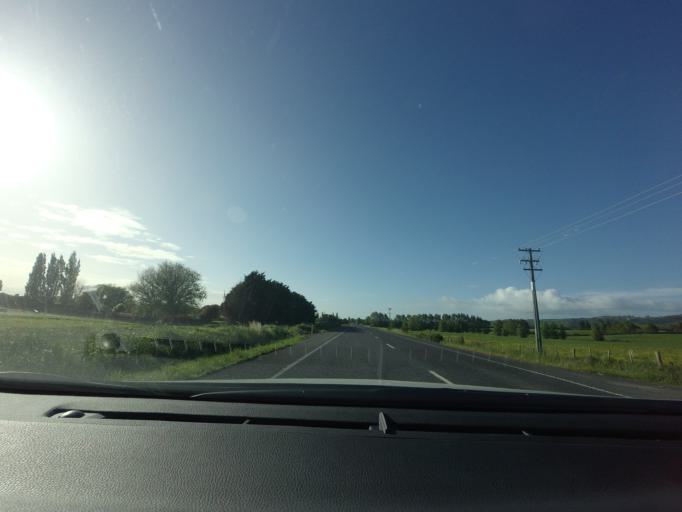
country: NZ
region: Waikato
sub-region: Hauraki District
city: Ngatea
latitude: -37.4223
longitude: 175.4859
